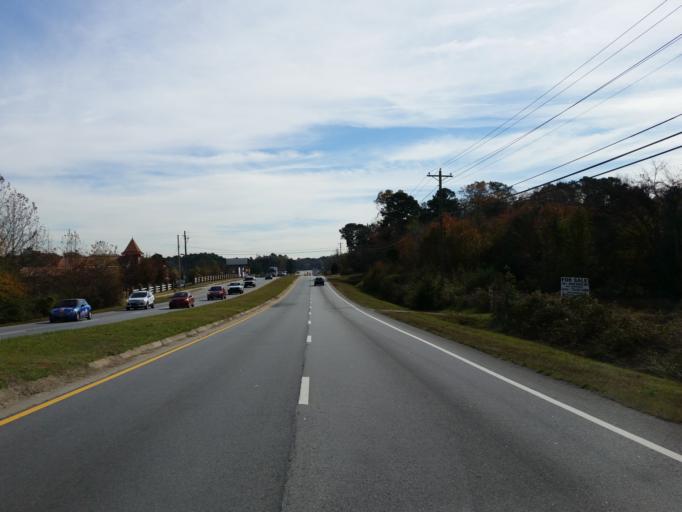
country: US
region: Georgia
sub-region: Douglas County
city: Lithia Springs
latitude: 33.7368
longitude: -84.6732
